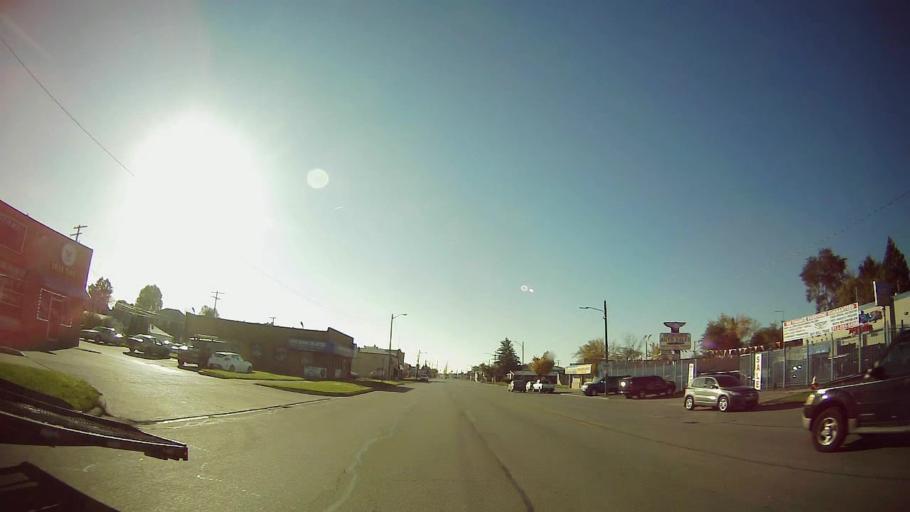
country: US
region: Michigan
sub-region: Wayne County
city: Dearborn
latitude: 42.3461
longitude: -83.1963
